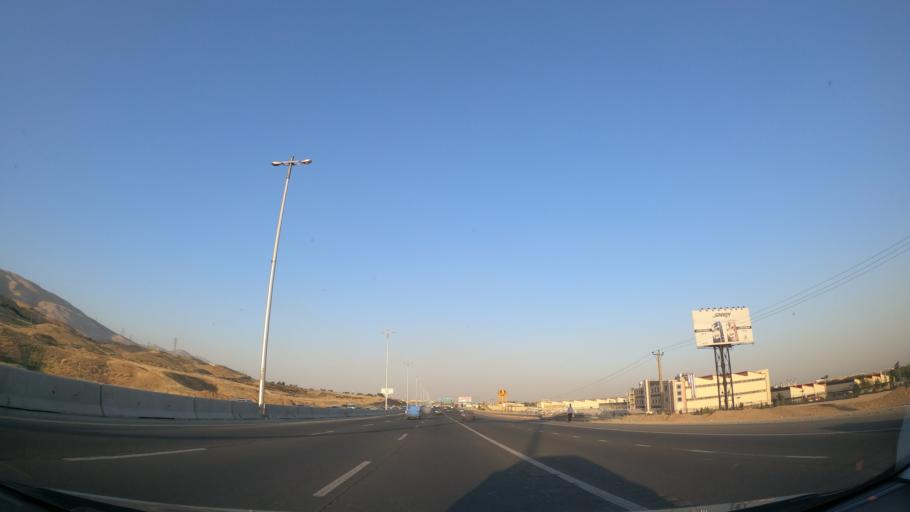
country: IR
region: Tehran
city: Shahr-e Qods
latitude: 35.7429
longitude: 51.1061
